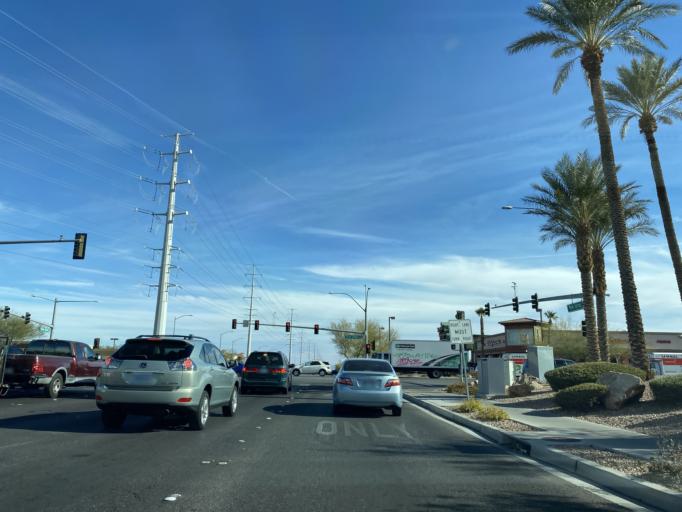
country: US
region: Nevada
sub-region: Clark County
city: Enterprise
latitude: 36.0554
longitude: -115.2798
